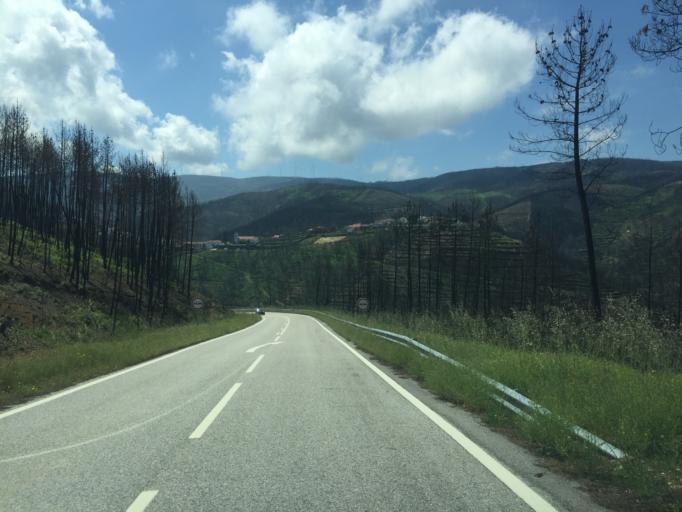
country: PT
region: Coimbra
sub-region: Pampilhosa da Serra
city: Pampilhosa da Serra
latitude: 39.9827
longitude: -7.9672
